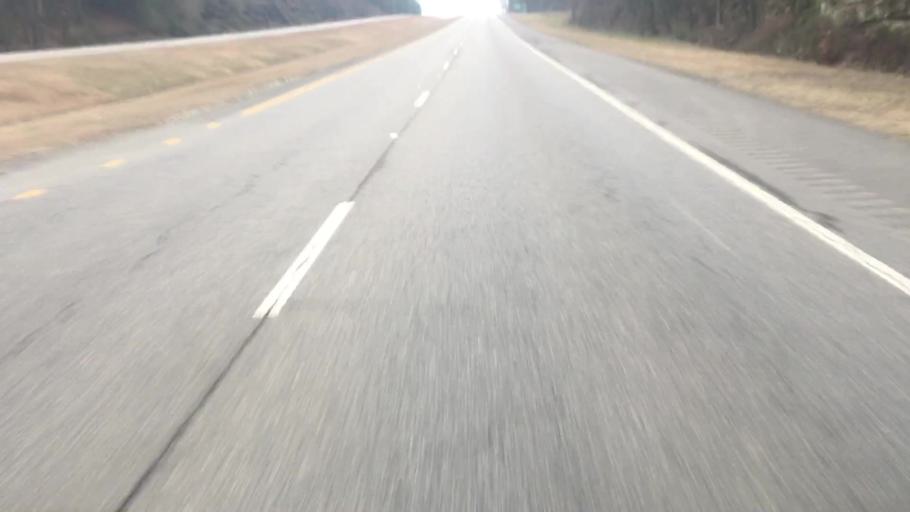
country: US
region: Alabama
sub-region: Walker County
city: Sumiton
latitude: 33.7688
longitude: -87.0715
